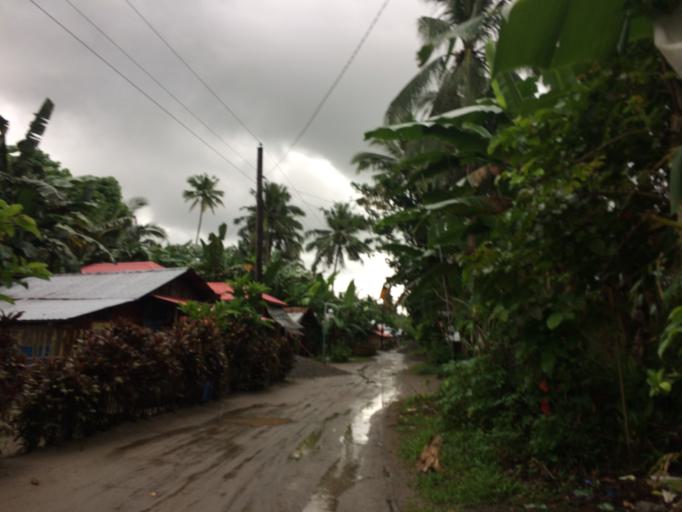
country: PH
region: Eastern Visayas
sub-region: Province of Leyte
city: Bugho
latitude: 10.8028
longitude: 124.9702
